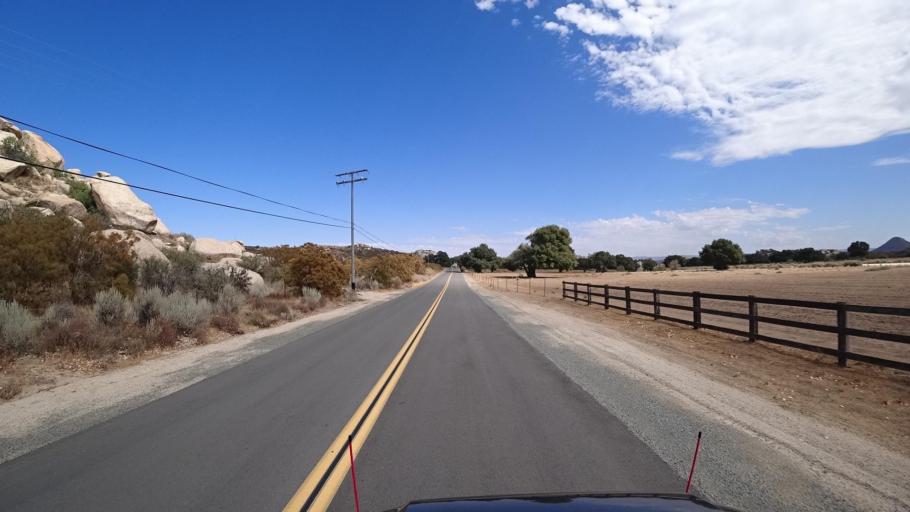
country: MX
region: Baja California
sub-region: Tecate
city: Cereso del Hongo
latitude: 32.6452
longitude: -116.2842
